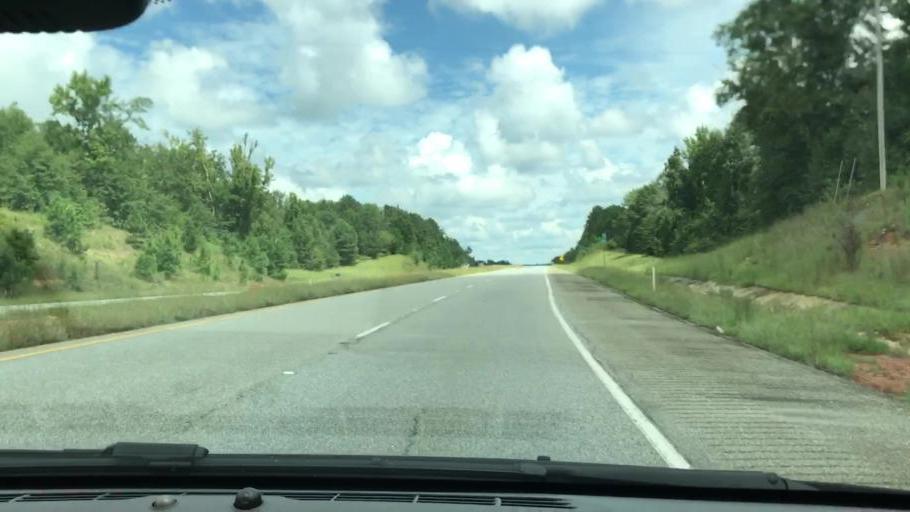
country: US
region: Georgia
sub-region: Stewart County
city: Lumpkin
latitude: 32.1631
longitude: -84.8307
